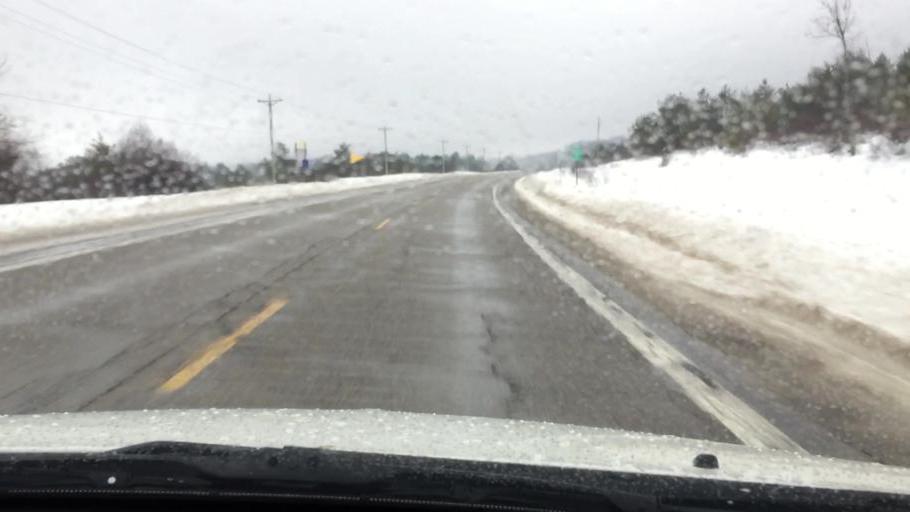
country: US
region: Michigan
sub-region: Charlevoix County
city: East Jordan
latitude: 45.1186
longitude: -85.1296
